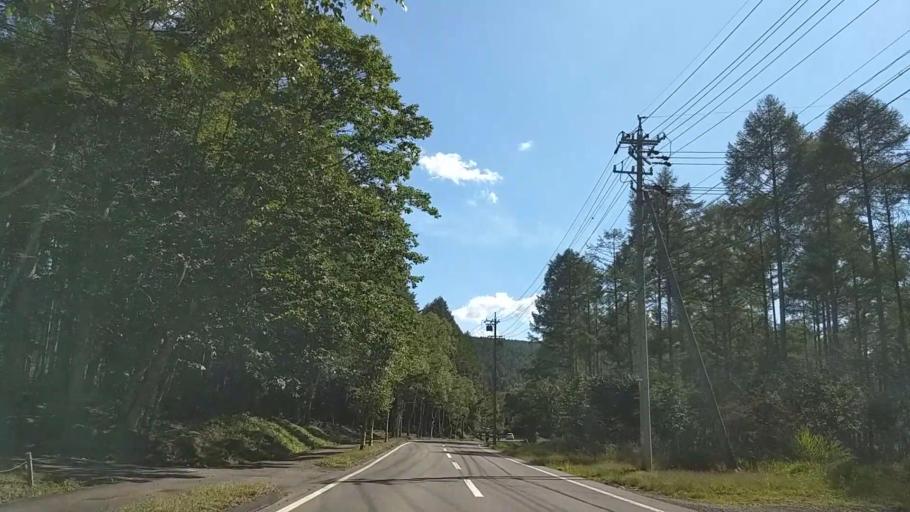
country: JP
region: Nagano
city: Chino
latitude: 36.1170
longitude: 138.2612
